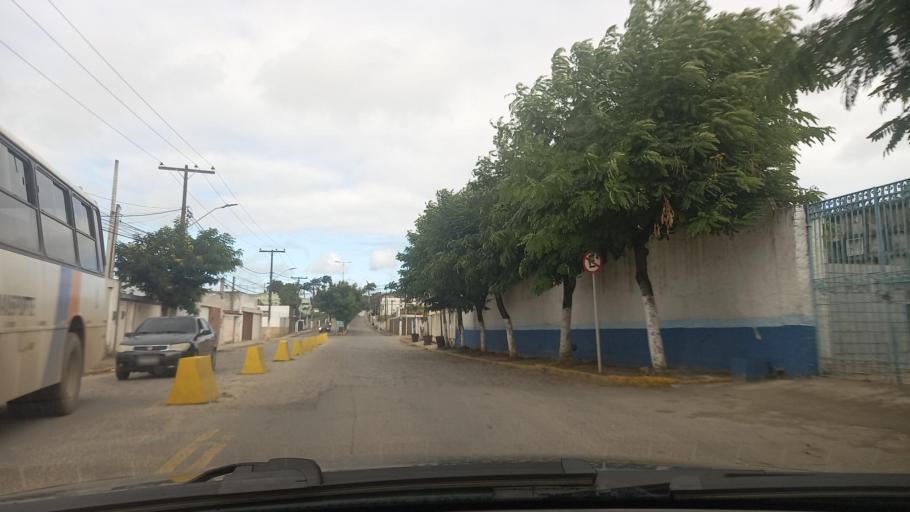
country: BR
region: Pernambuco
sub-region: Vitoria De Santo Antao
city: Vitoria de Santo Antao
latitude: -8.1199
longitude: -35.3035
